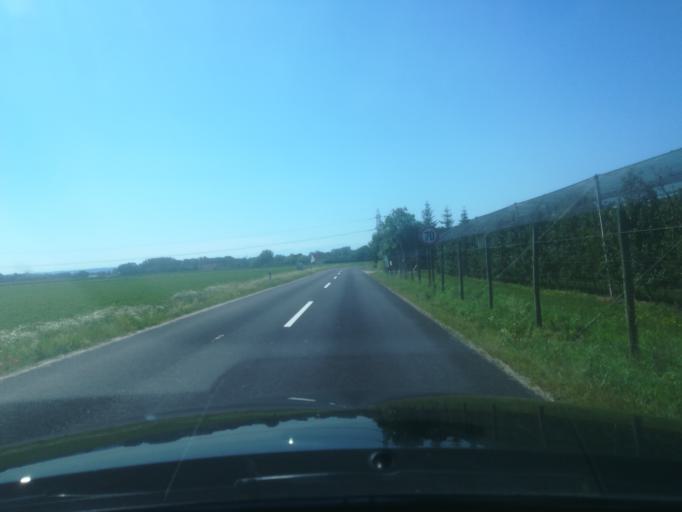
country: AT
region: Upper Austria
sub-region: Wels-Land
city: Holzhausen
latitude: 48.2159
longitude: 14.0889
